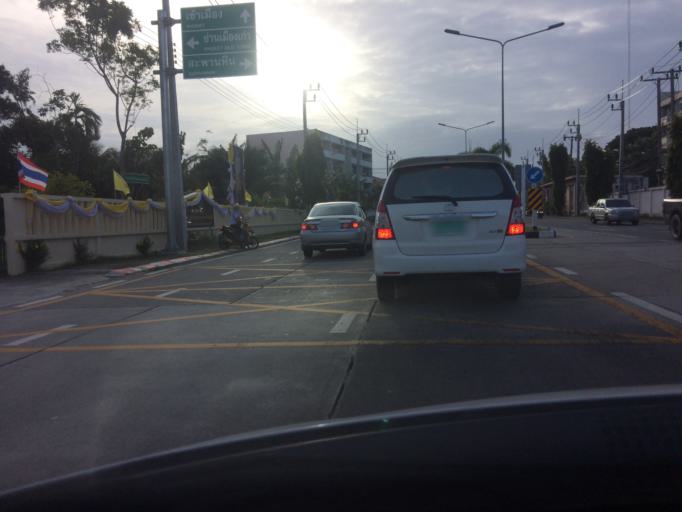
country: TH
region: Phuket
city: Ban Talat Nua
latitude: 7.8693
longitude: 98.3901
